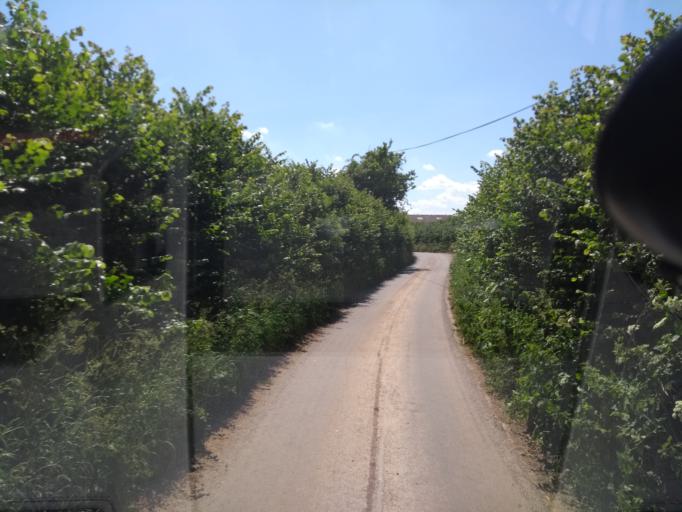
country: GB
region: England
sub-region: Somerset
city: North Petherton
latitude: 51.0621
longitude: -3.0021
